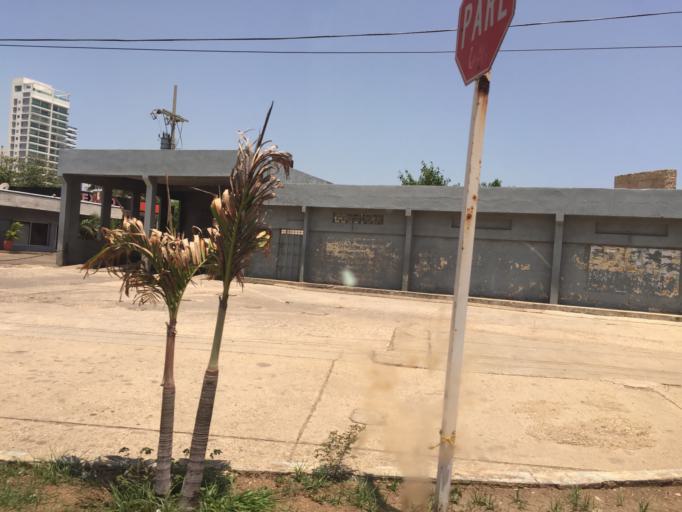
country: CO
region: Bolivar
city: Cartagena
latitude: 10.4169
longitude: -75.5428
